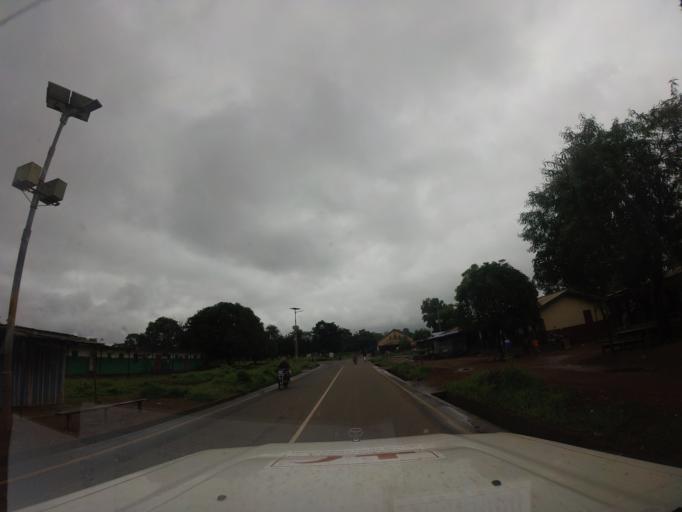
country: SL
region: Northern Province
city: Kambia
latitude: 9.1129
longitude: -12.9249
